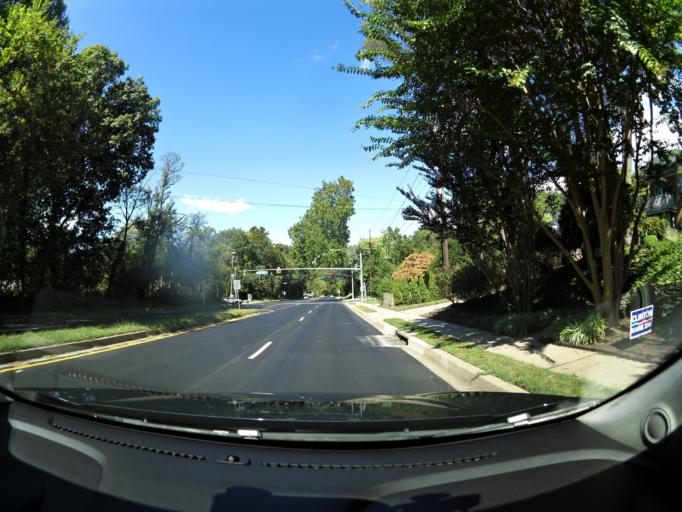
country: US
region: Maryland
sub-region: Montgomery County
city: Somerset
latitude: 38.9552
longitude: -77.1050
